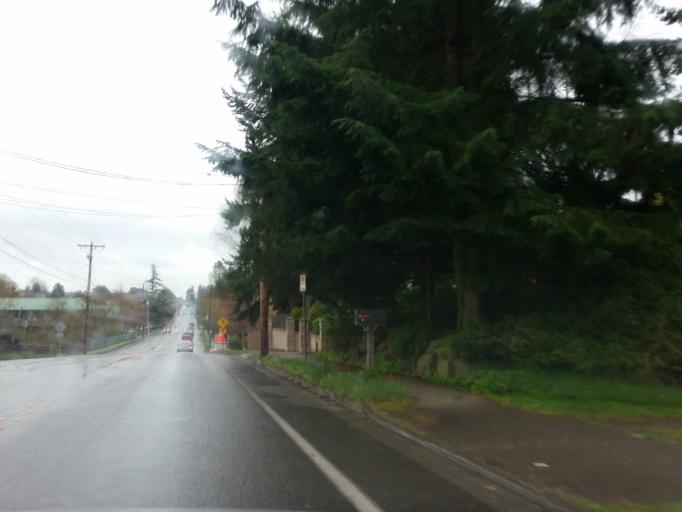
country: US
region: Washington
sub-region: Snohomish County
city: Lynnwood
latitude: 47.8174
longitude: -122.3044
